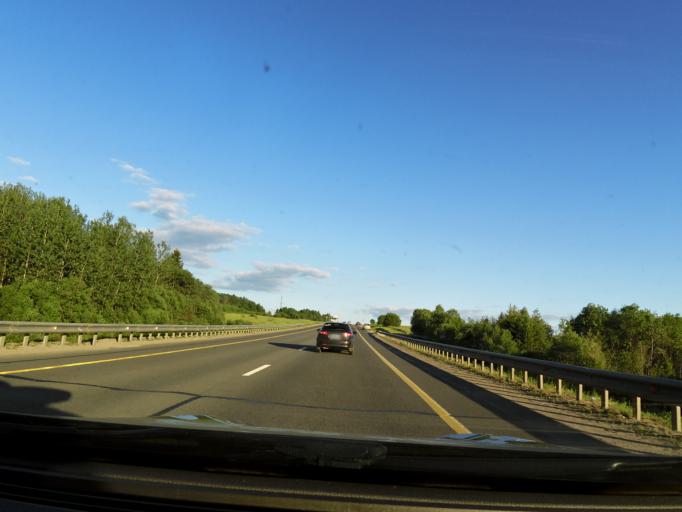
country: RU
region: Vologda
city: Vologda
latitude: 59.1156
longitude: 39.9755
